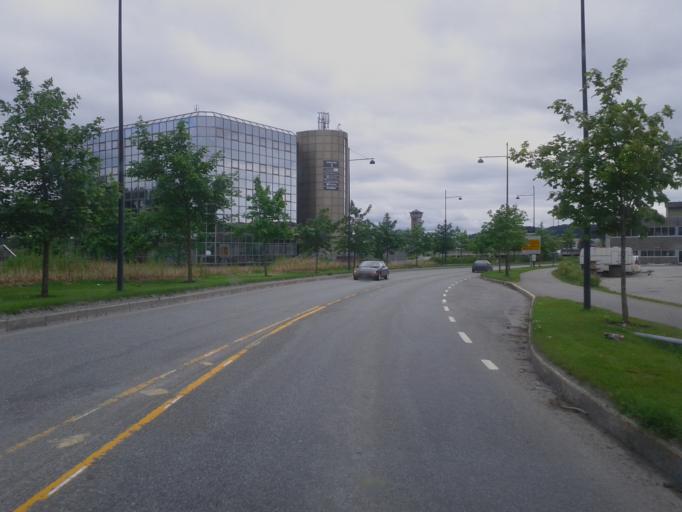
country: NO
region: Nord-Trondelag
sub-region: Steinkjer
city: Steinkjer
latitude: 64.0206
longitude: 11.4913
